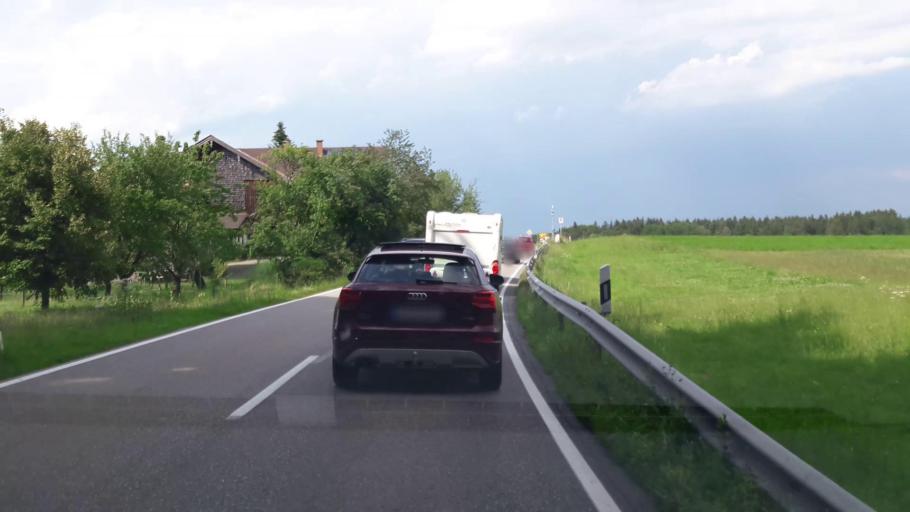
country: DE
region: Bavaria
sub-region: Upper Bavaria
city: Anger
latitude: 47.8249
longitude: 12.8395
